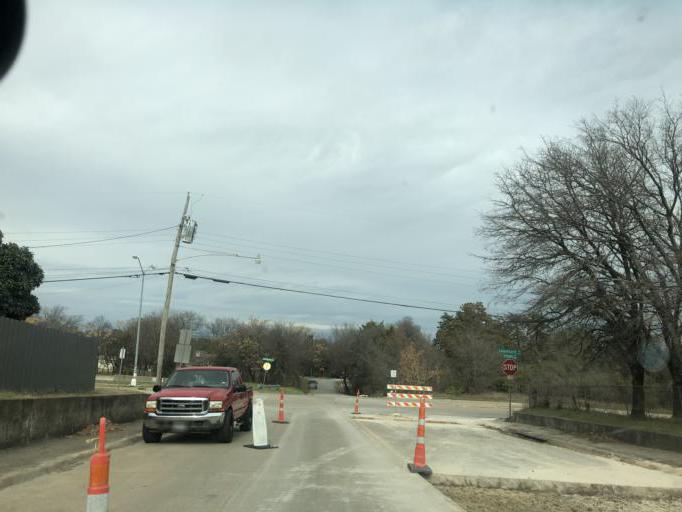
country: US
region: Texas
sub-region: Dallas County
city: Duncanville
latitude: 32.6745
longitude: -96.8291
